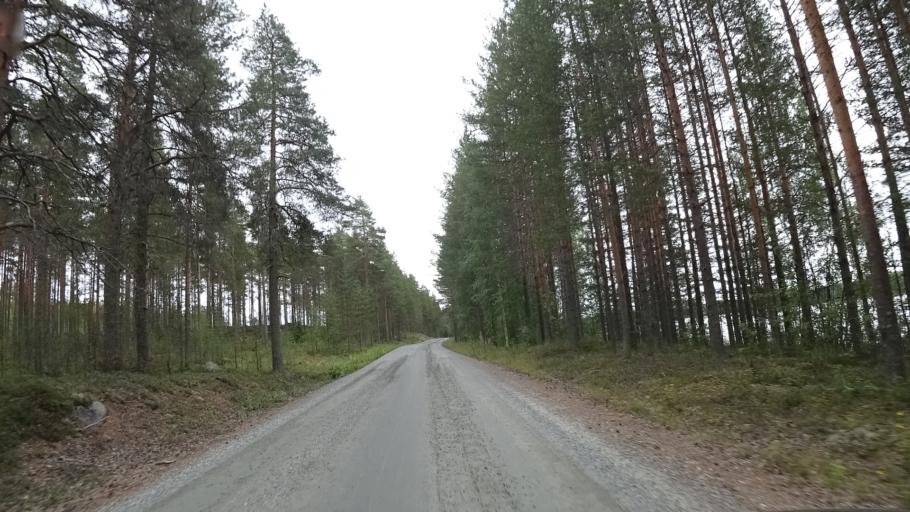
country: FI
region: North Karelia
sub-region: Pielisen Karjala
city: Lieksa
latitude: 63.3847
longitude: 30.3390
